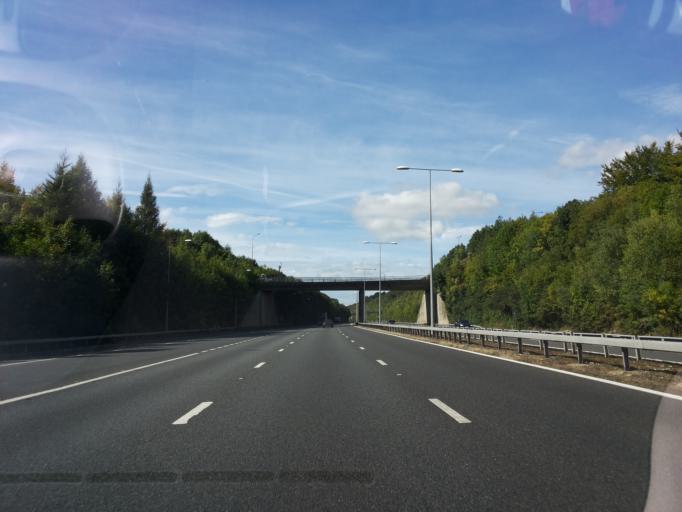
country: GB
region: England
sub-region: Kent
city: Borough Green
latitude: 51.3108
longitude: 0.3153
